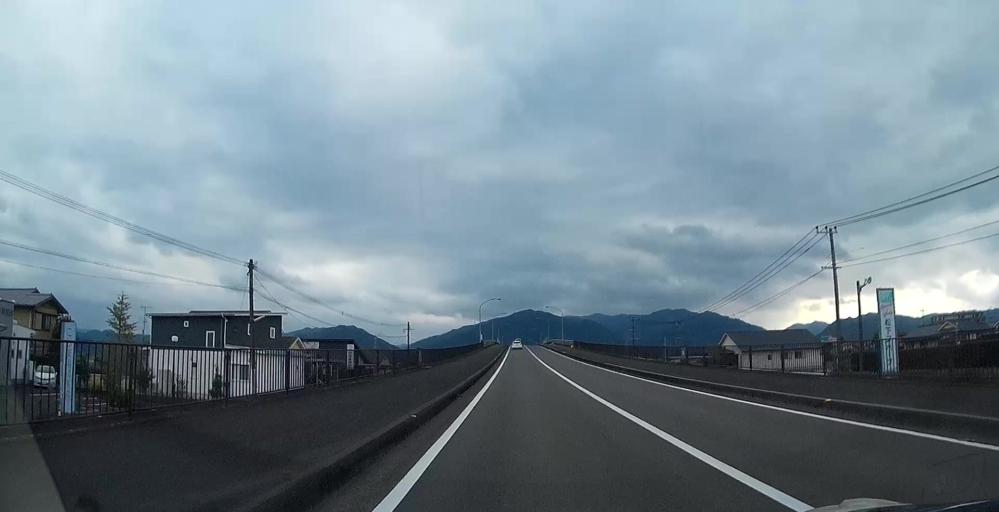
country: JP
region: Kagoshima
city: Izumi
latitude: 32.0794
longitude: 130.3453
